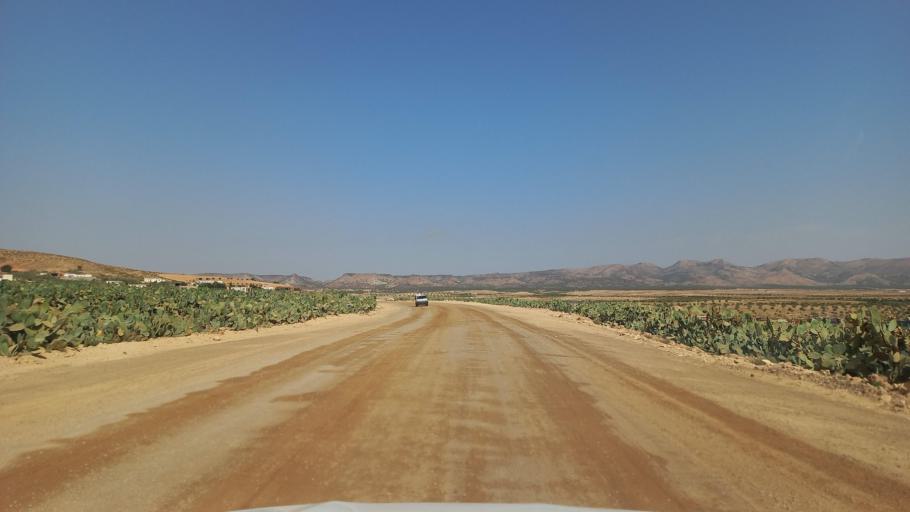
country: TN
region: Al Qasrayn
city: Sbiba
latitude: 35.3821
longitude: 9.0289
